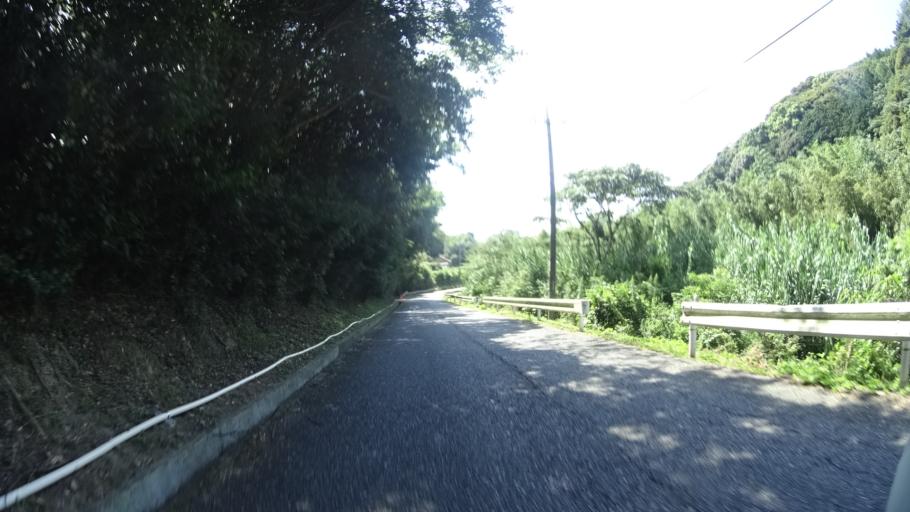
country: JP
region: Yamaguchi
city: Shimonoseki
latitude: 34.1058
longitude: 130.8688
